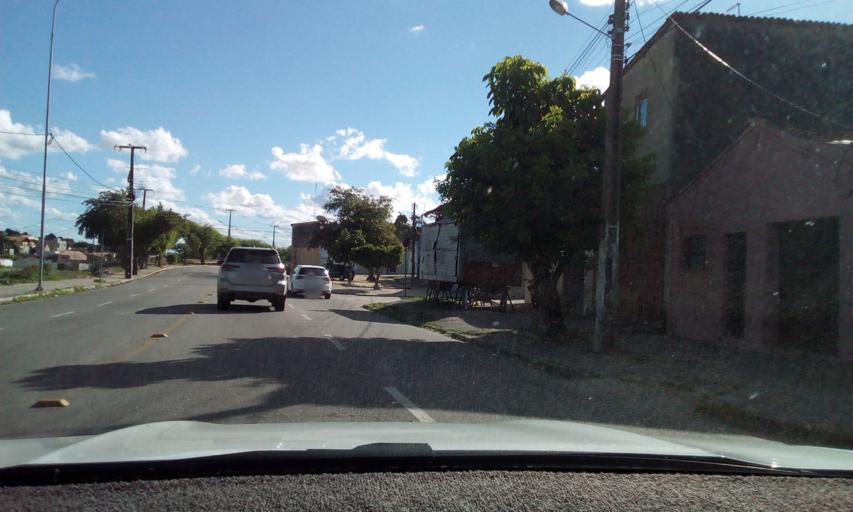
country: BR
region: Paraiba
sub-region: Campina Grande
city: Campina Grande
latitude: -7.2291
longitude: -35.8975
